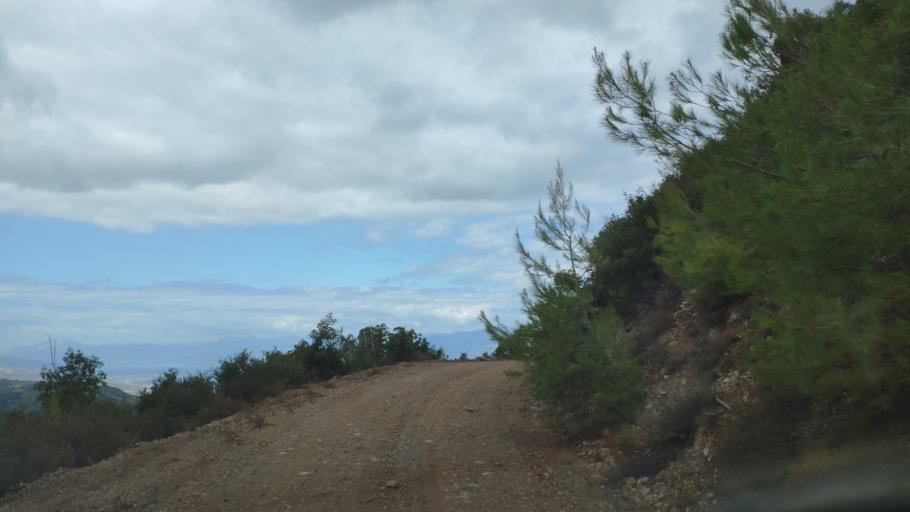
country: GR
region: West Greece
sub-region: Nomos Achaias
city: Temeni
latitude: 38.1723
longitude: 22.1551
